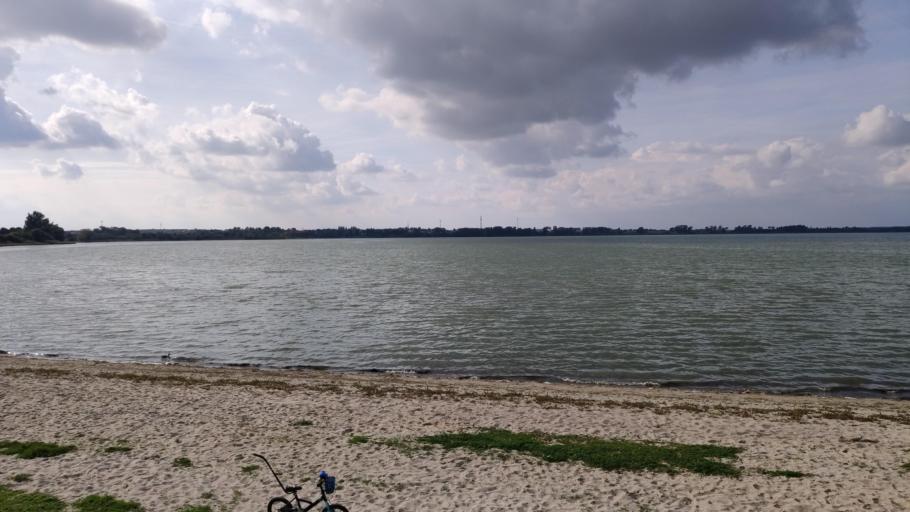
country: PL
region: Kujawsko-Pomorskie
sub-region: Powiat zninski
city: Znin
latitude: 52.8546
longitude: 17.7514
